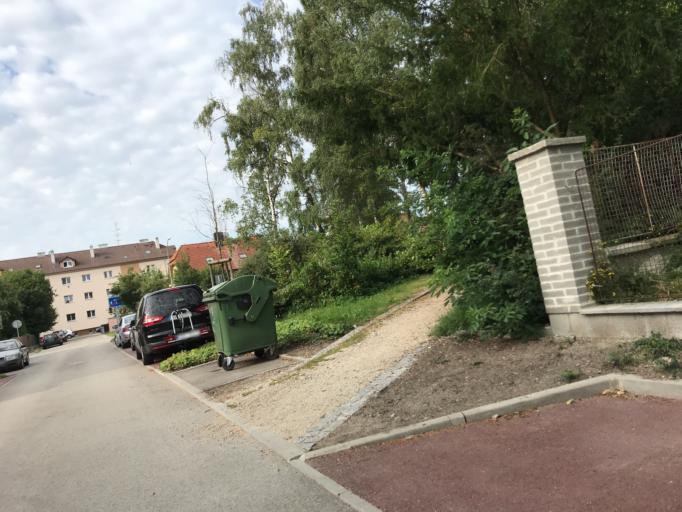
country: CZ
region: Jihocesky
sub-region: Okres Jindrichuv Hradec
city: Trebon
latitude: 49.0067
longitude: 14.7641
